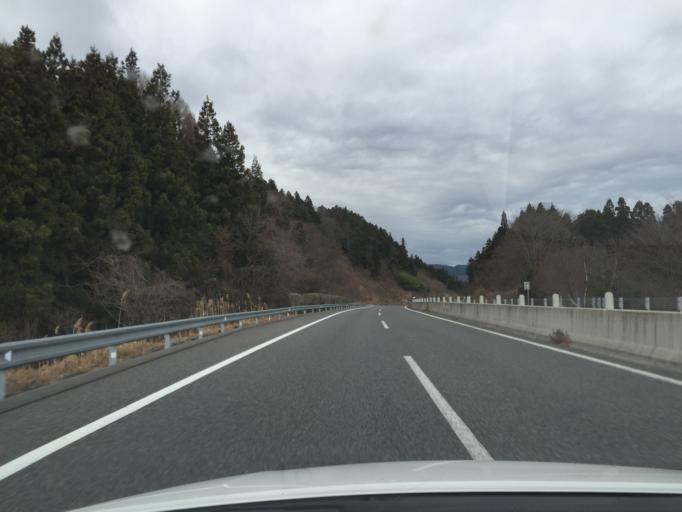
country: JP
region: Fukushima
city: Funehikimachi-funehiki
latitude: 37.3067
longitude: 140.6115
